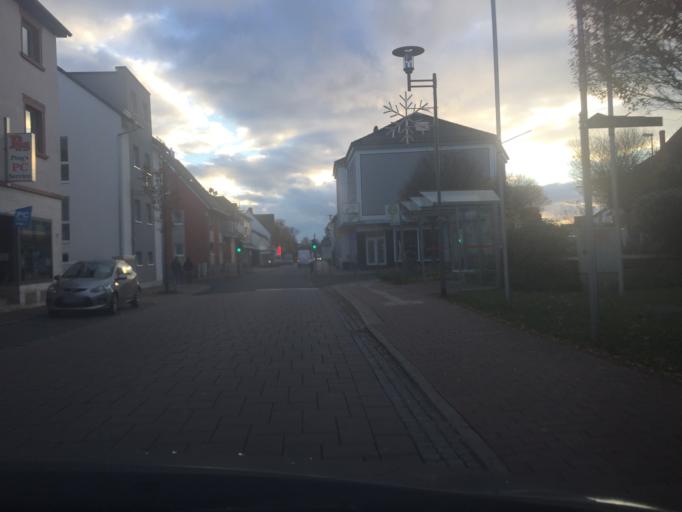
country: DE
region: Bavaria
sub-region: Regierungsbezirk Unterfranken
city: Goldbach
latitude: 49.9963
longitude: 9.1780
